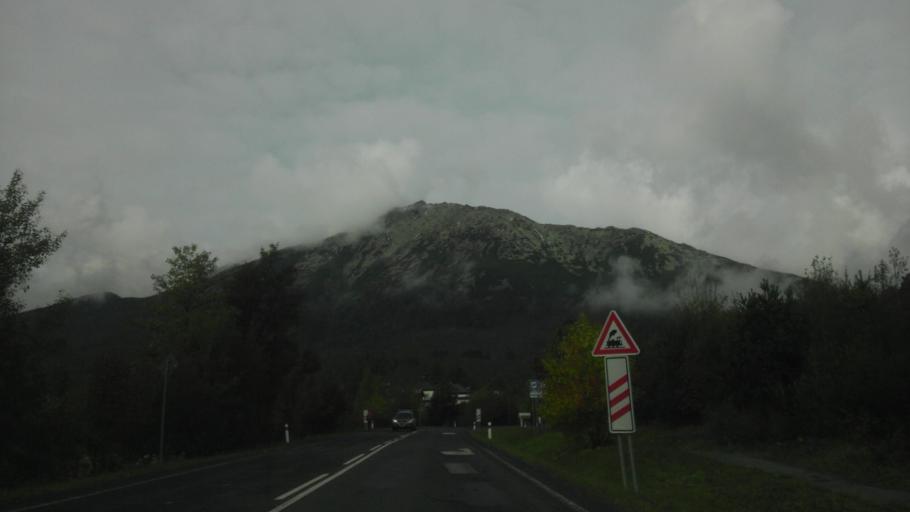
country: SK
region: Presovsky
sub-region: Okres Poprad
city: Vysoke Tatry
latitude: 49.1377
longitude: 20.2279
